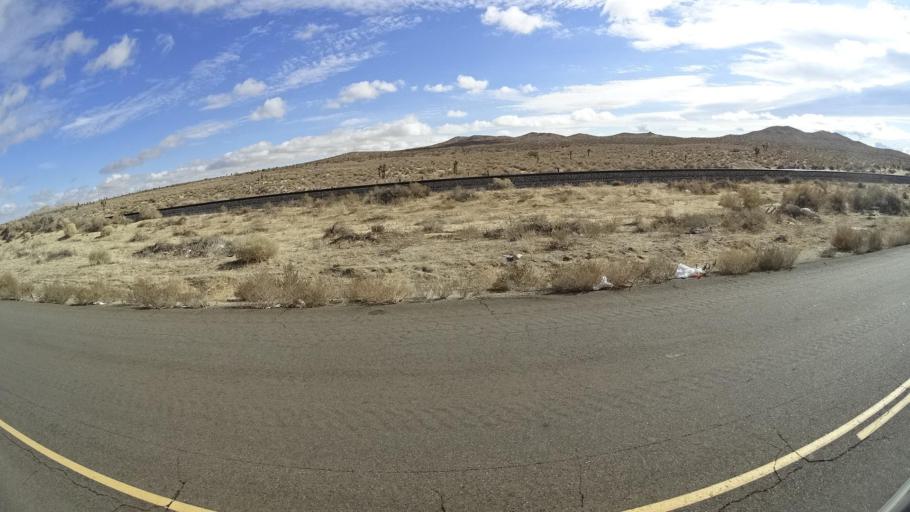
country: US
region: California
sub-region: Kern County
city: Rosamond
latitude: 34.9000
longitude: -118.1582
